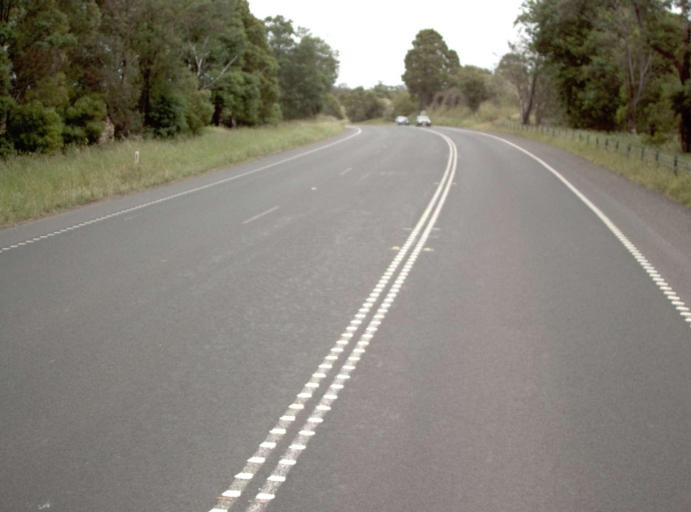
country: AU
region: Victoria
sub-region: Bass Coast
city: North Wonthaggi
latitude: -38.4240
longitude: 145.8083
